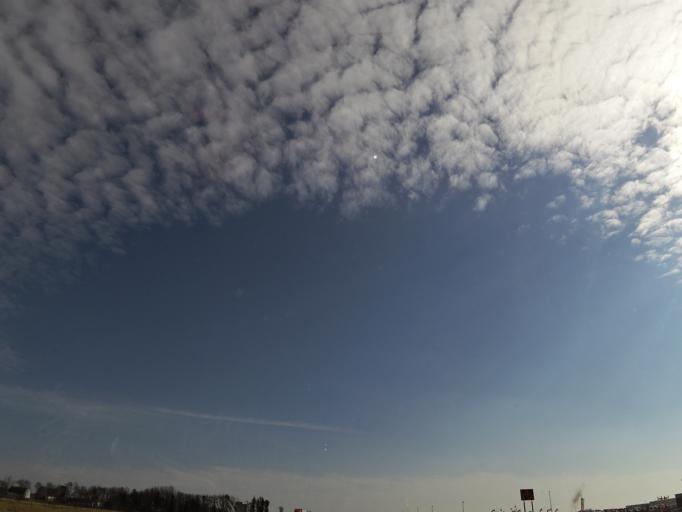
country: US
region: Minnesota
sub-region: Steele County
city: Medford
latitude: 44.1607
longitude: -93.2578
